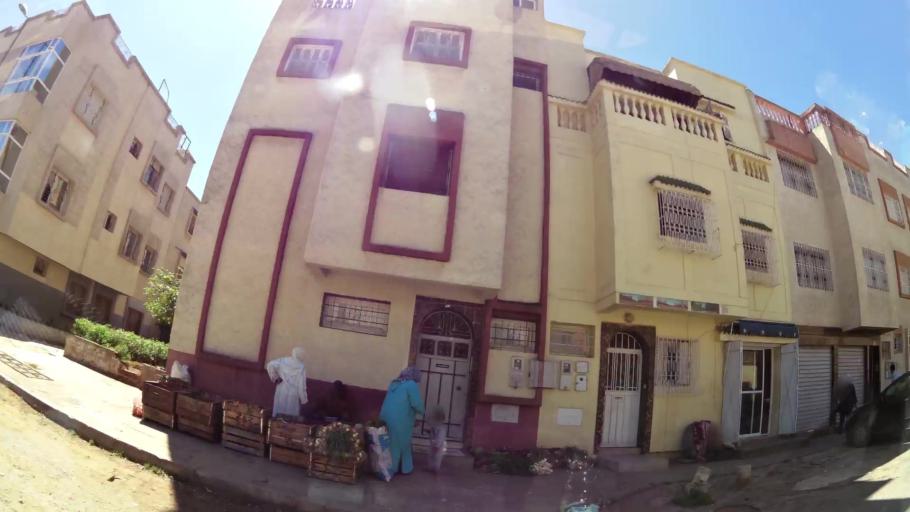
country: MA
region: Meknes-Tafilalet
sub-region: Meknes
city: Meknes
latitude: 33.9002
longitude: -5.5158
